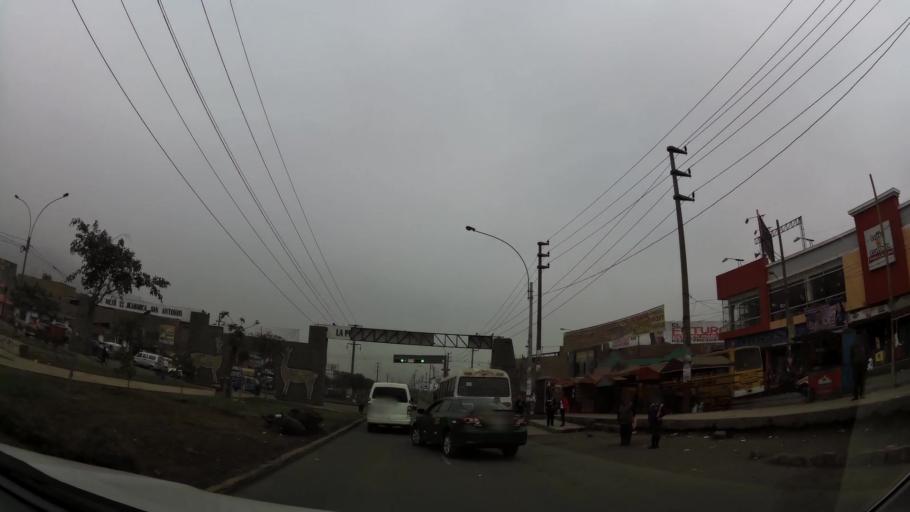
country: PE
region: Lima
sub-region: Lima
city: Urb. Santo Domingo
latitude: -11.9322
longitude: -76.9690
